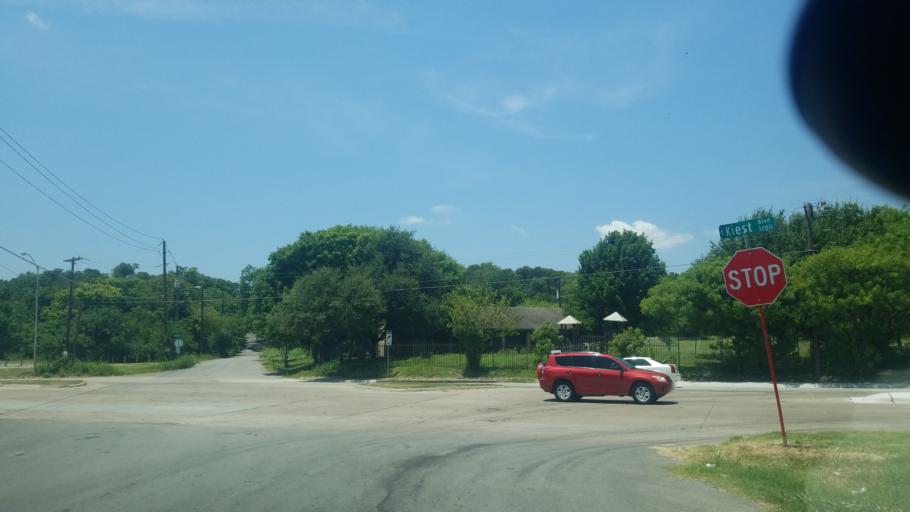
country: US
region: Texas
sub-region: Dallas County
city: Dallas
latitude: 32.7297
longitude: -96.7850
